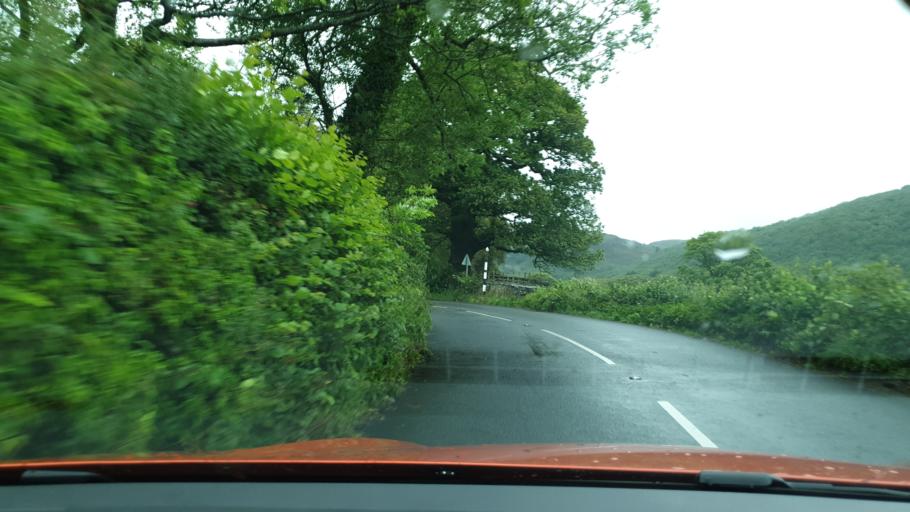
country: GB
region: England
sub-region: Cumbria
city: Ulverston
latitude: 54.2882
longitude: -3.0934
